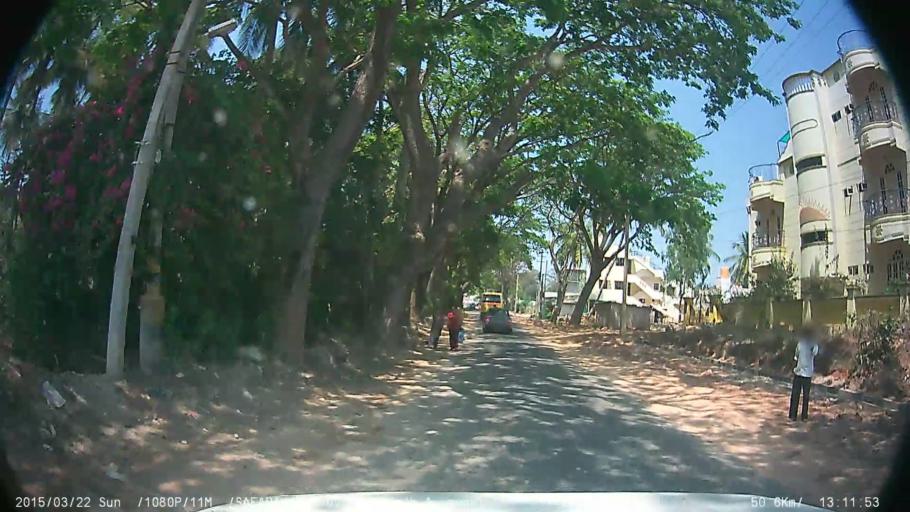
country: IN
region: Karnataka
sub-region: Bangalore Urban
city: Anekal
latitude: 12.8091
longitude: 77.5783
